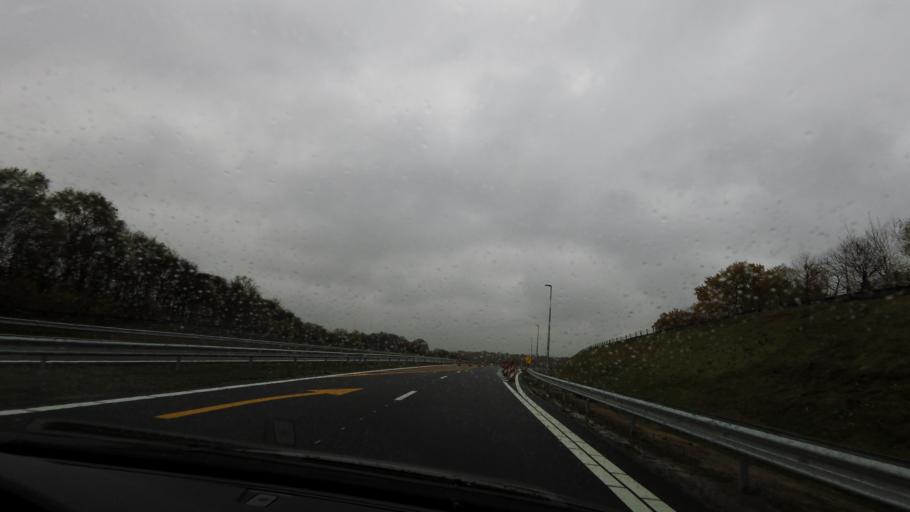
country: NL
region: Limburg
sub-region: Gemeente Brunssum
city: Brunssum
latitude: 50.9584
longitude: 5.9663
